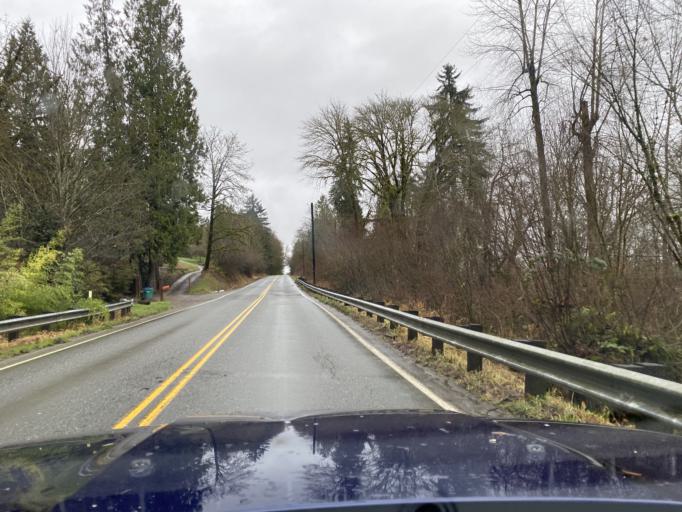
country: US
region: Washington
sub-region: King County
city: Duvall
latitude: 47.7564
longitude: -122.0046
